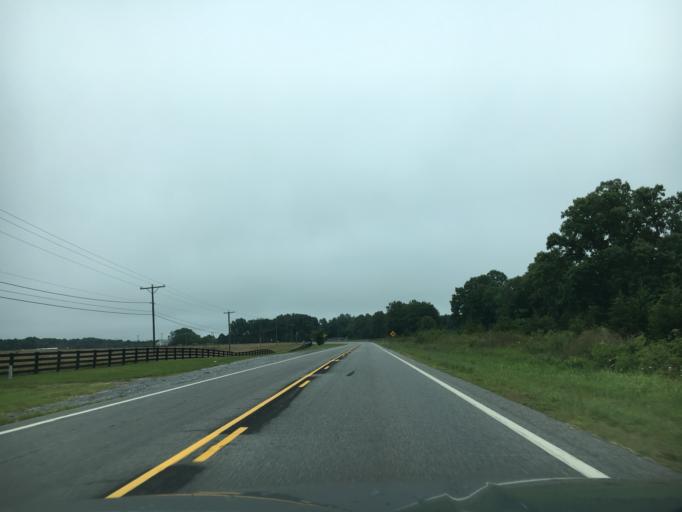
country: US
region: Virginia
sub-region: Campbell County
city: Brookneal
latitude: 37.0794
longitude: -78.9856
